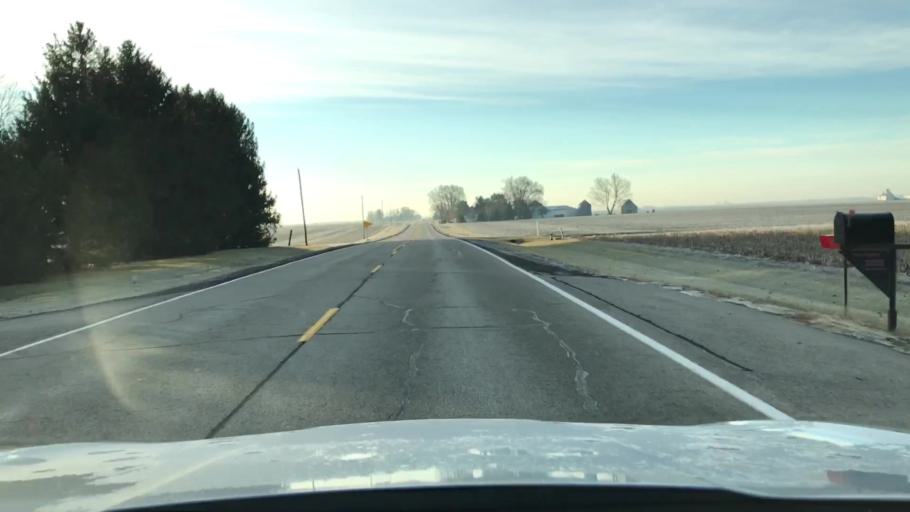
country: US
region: Illinois
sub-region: McLean County
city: Hudson
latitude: 40.6137
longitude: -88.9455
